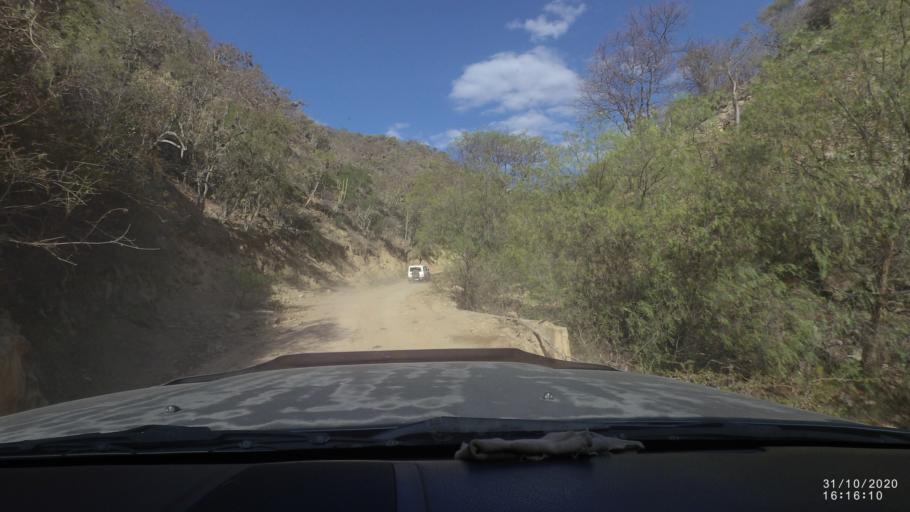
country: BO
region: Chuquisaca
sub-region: Provincia Zudanez
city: Mojocoya
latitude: -18.3899
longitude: -64.6101
